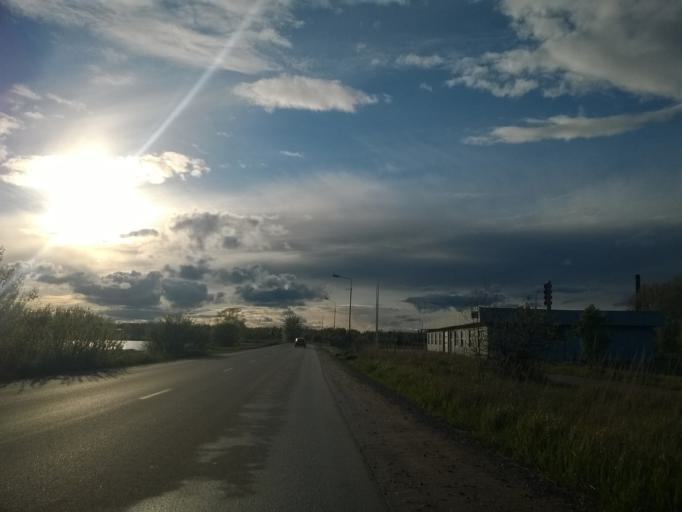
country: LV
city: Tireli
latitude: 56.9346
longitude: 23.6054
